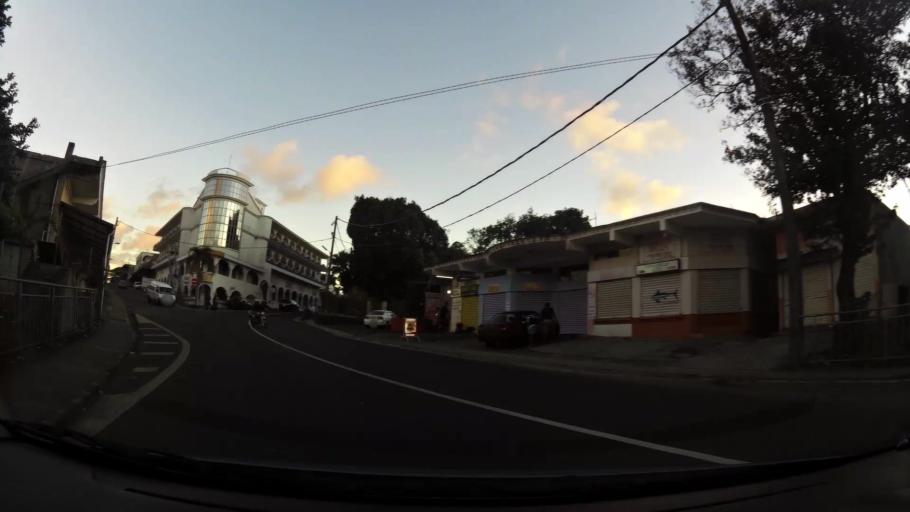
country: MU
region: Moka
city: Verdun
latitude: -20.2227
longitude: 57.5361
